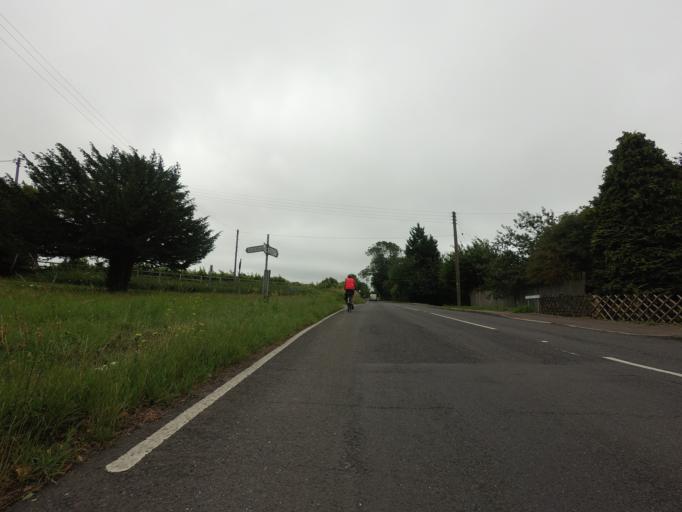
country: GB
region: England
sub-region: Kent
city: Meopham
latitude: 51.3802
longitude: 0.3517
